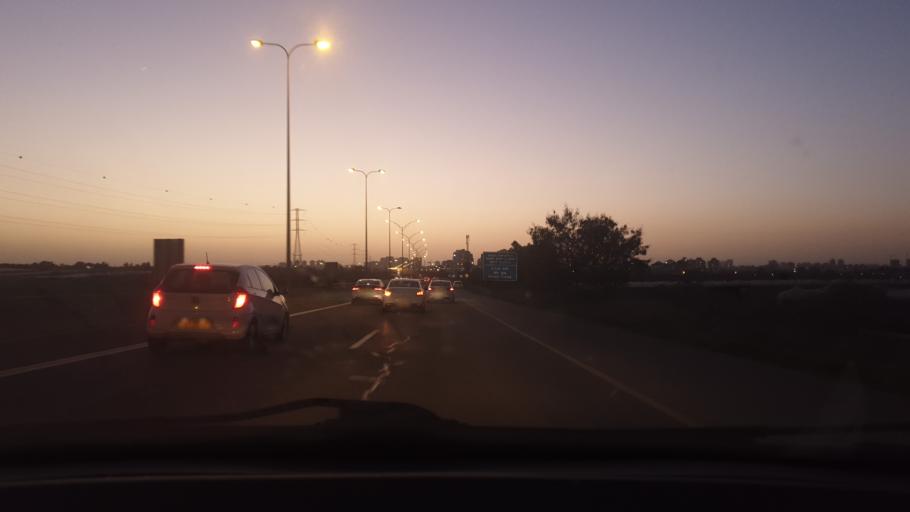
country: IL
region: Central District
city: Nehalim
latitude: 32.0681
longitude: 34.9288
